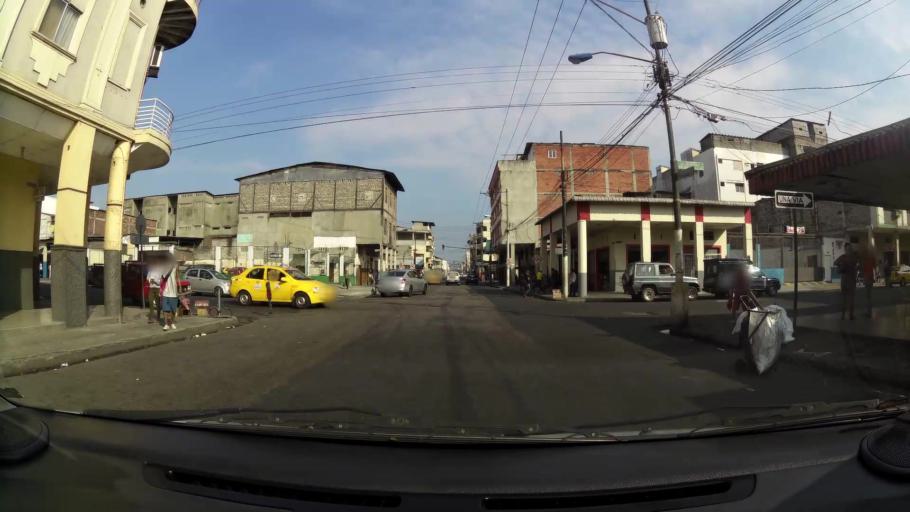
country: EC
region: Guayas
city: Guayaquil
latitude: -2.1954
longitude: -79.8895
